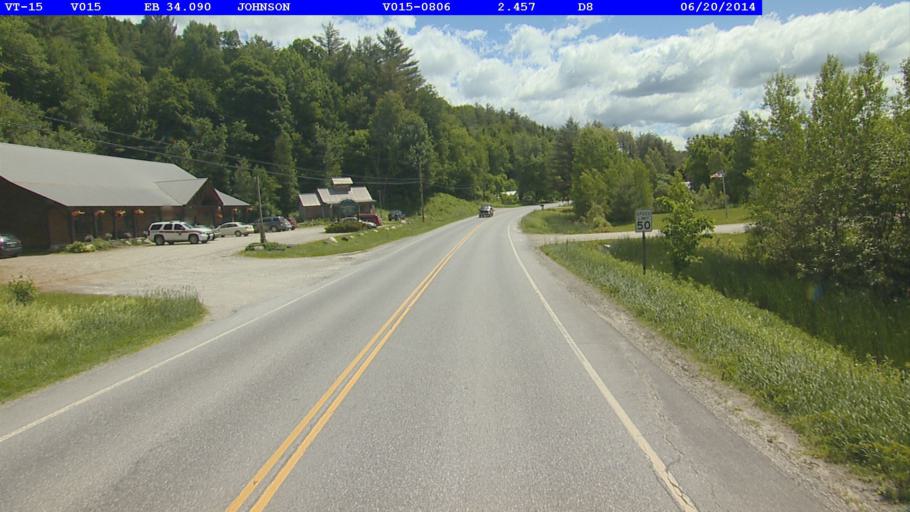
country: US
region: Vermont
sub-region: Lamoille County
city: Johnson
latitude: 44.6430
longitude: -72.7077
